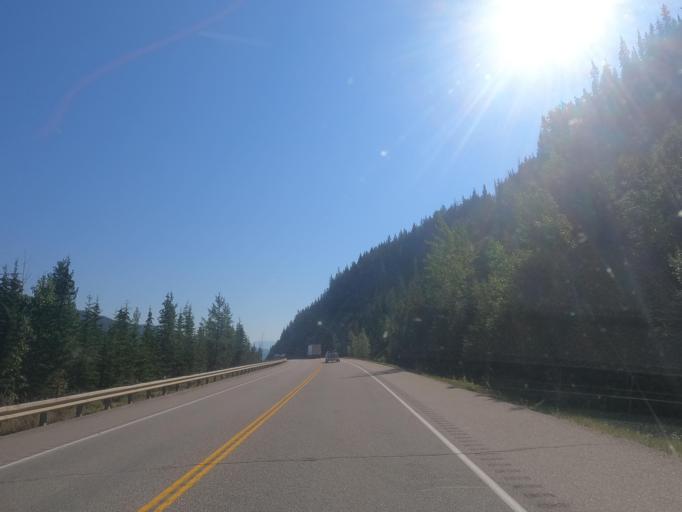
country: CA
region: Alberta
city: Jasper Park Lodge
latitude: 52.8770
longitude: -118.3405
